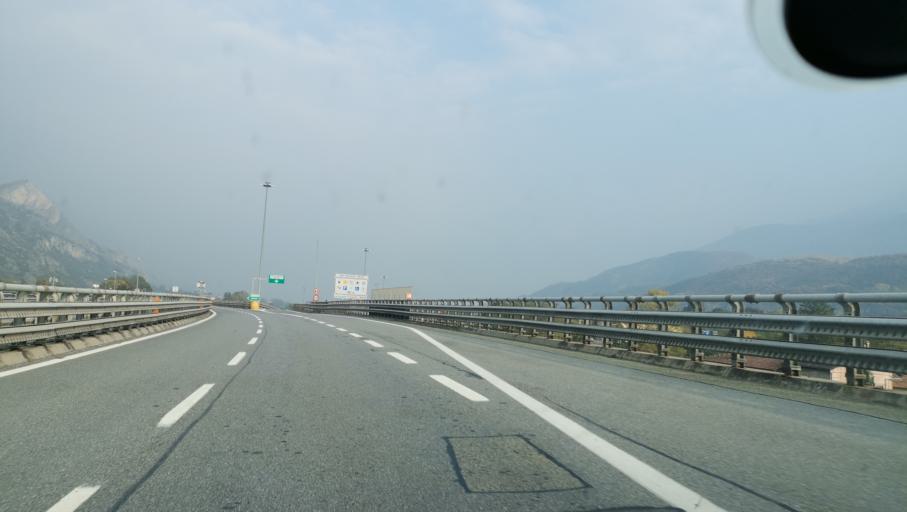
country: IT
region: Piedmont
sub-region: Provincia di Torino
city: Meana di Susa
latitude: 45.1357
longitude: 7.0815
